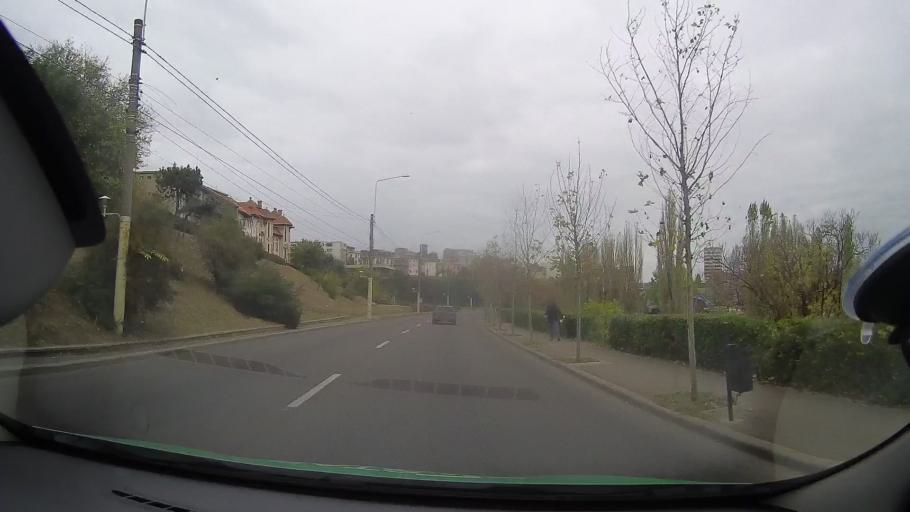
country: RO
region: Constanta
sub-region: Municipiul Constanta
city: Constanta
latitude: 44.1739
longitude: 28.6557
